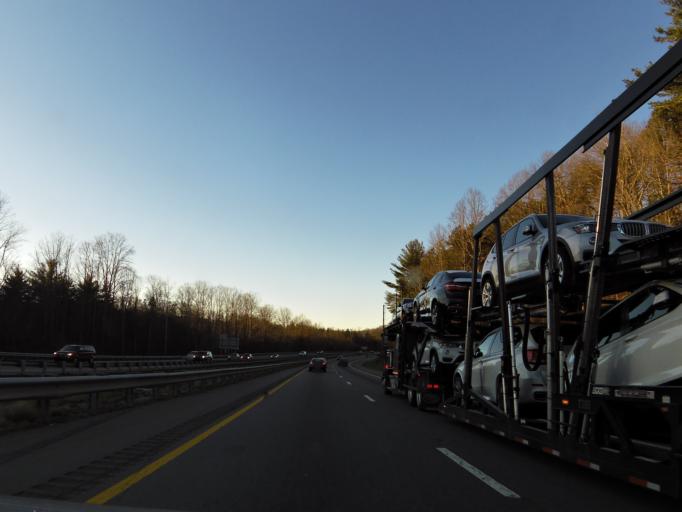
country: US
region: North Carolina
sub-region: Buncombe County
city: Avery Creek
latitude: 35.4849
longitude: -82.5596
